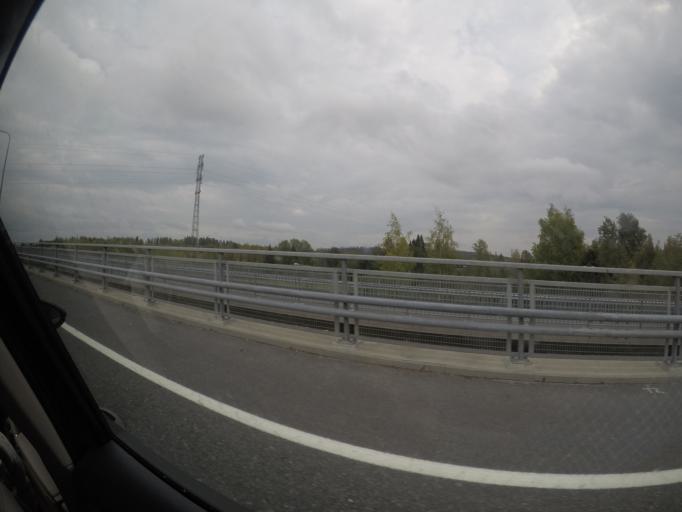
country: FI
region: Haeme
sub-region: Haemeenlinna
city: Haemeenlinna
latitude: 61.0213
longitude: 24.4220
